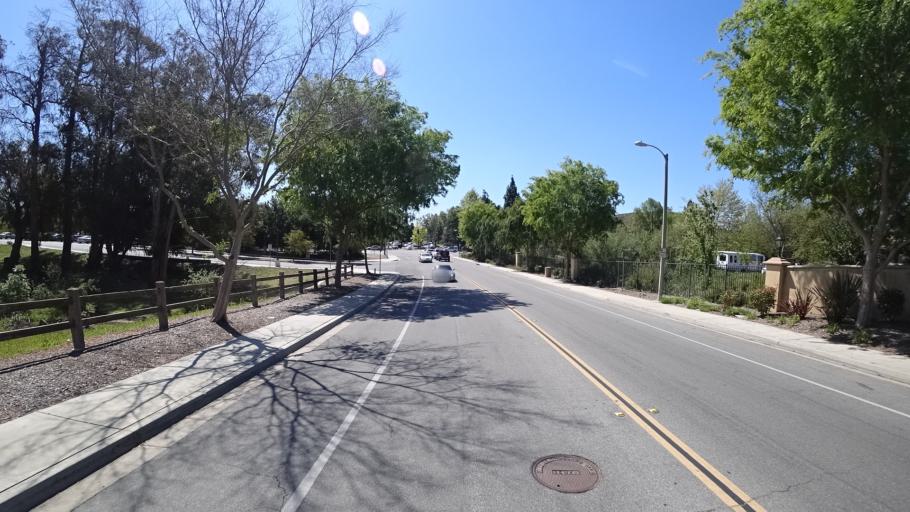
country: US
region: California
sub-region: Ventura County
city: Moorpark
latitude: 34.2260
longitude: -118.8814
